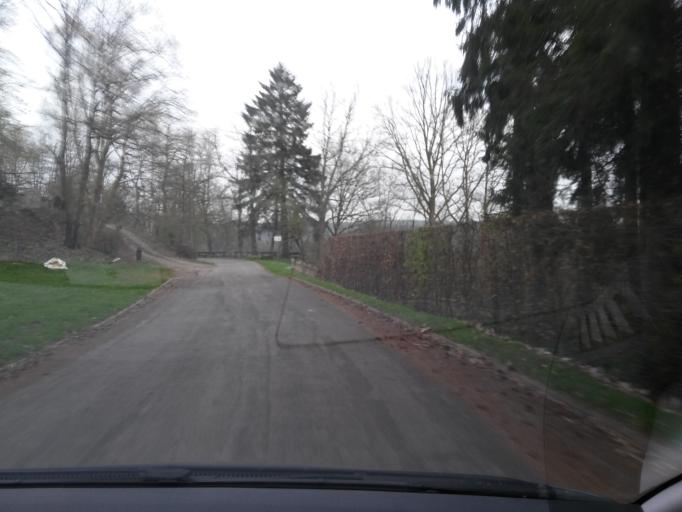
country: BE
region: Wallonia
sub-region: Province du Luxembourg
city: Herbeumont
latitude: 49.7735
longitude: 5.2409
